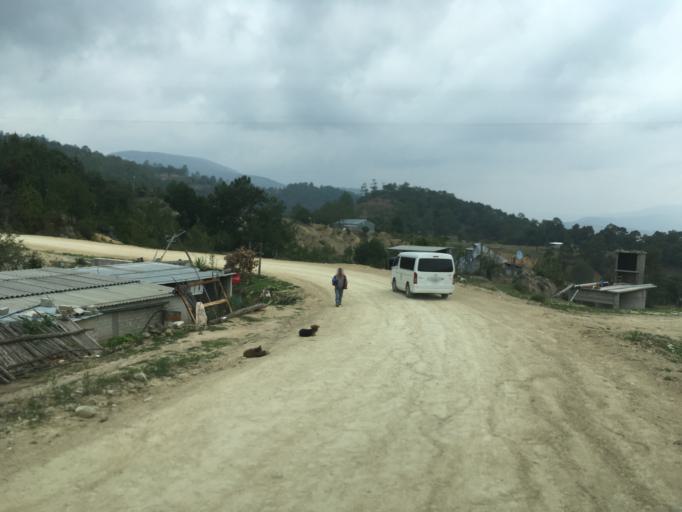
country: MX
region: Oaxaca
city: Santiago Tilantongo
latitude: 17.1974
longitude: -97.2817
